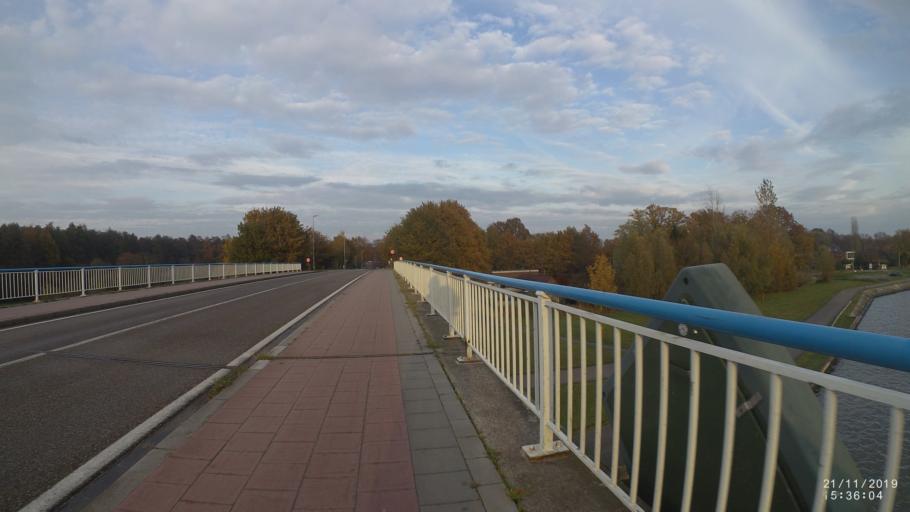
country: BE
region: Flanders
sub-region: Provincie Limburg
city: Hasselt
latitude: 50.9545
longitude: 5.3128
